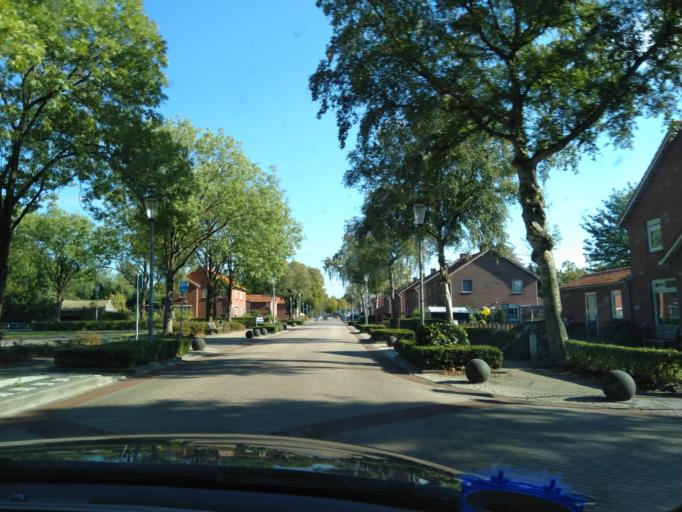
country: NL
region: Groningen
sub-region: Gemeente Veendam
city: Veendam
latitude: 53.0867
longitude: 6.8615
